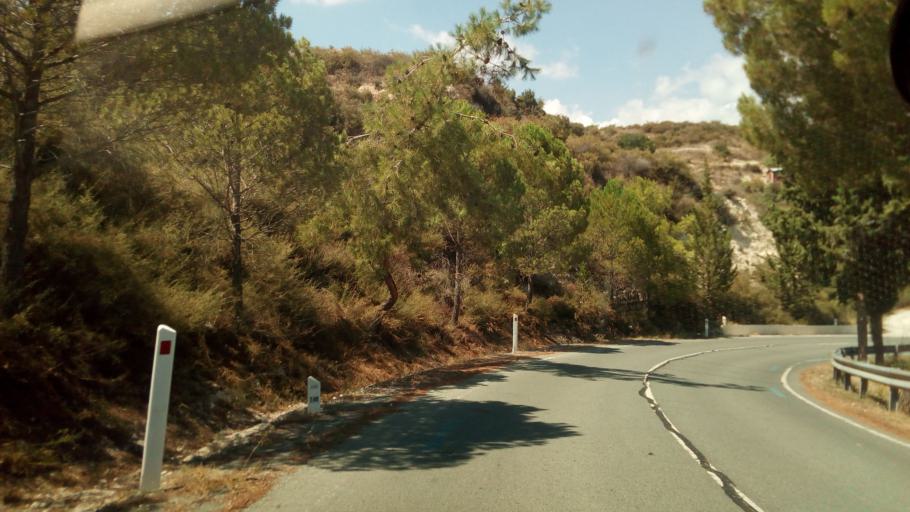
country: CY
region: Limassol
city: Pachna
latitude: 34.8300
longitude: 32.8460
